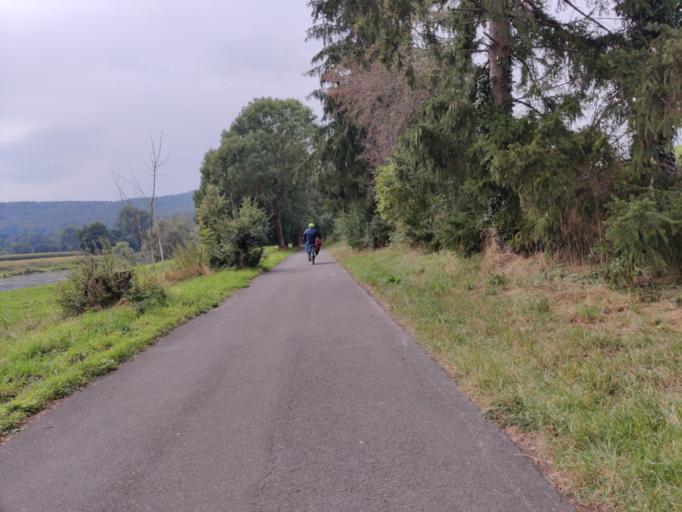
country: DE
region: Lower Saxony
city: Holzminden
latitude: 51.8164
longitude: 9.4130
